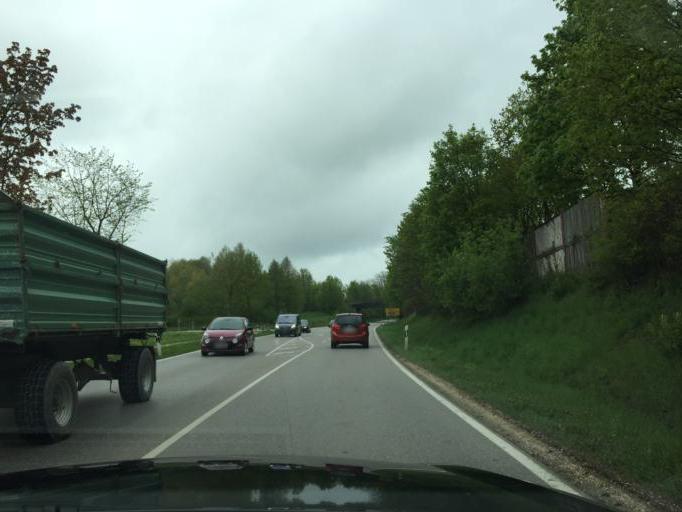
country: DE
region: Bavaria
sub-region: Swabia
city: Wertingen
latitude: 48.5548
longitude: 10.6722
